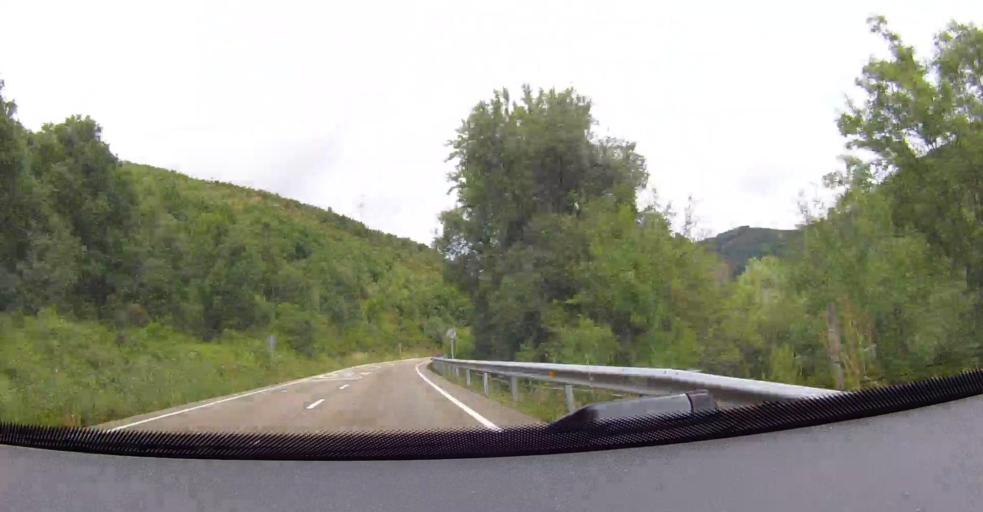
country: ES
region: Castille and Leon
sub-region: Provincia de Leon
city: Bonar
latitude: 42.8991
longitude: -5.3147
